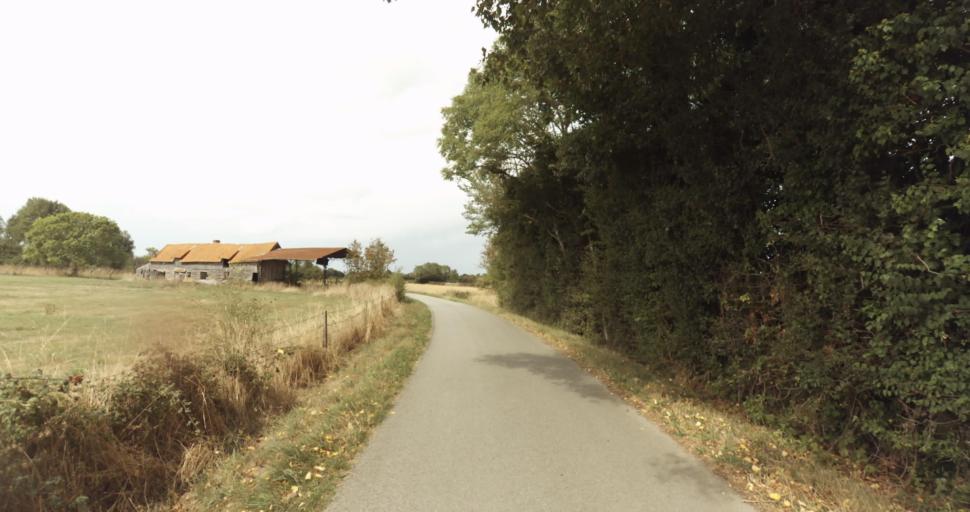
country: FR
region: Lower Normandy
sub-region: Departement du Calvados
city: Orbec
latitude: 48.9173
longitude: 0.3806
